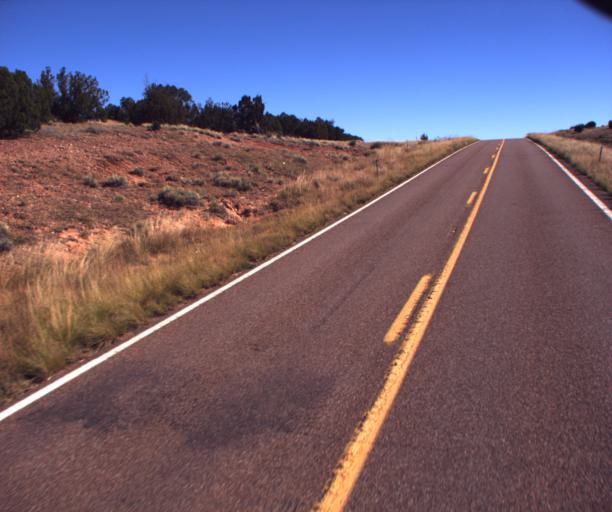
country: US
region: Arizona
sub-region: Navajo County
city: Heber-Overgaard
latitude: 34.4576
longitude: -110.4397
